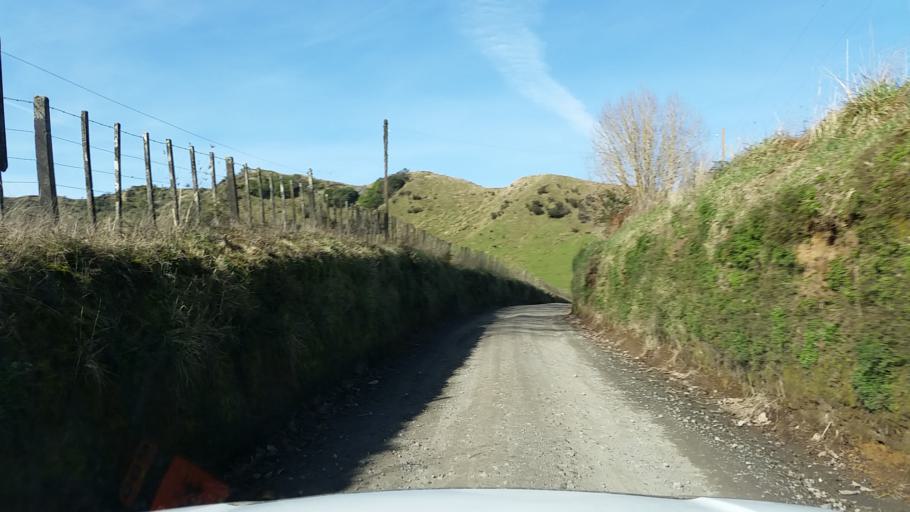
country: NZ
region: Taranaki
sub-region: South Taranaki District
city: Eltham
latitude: -39.3537
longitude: 174.5136
